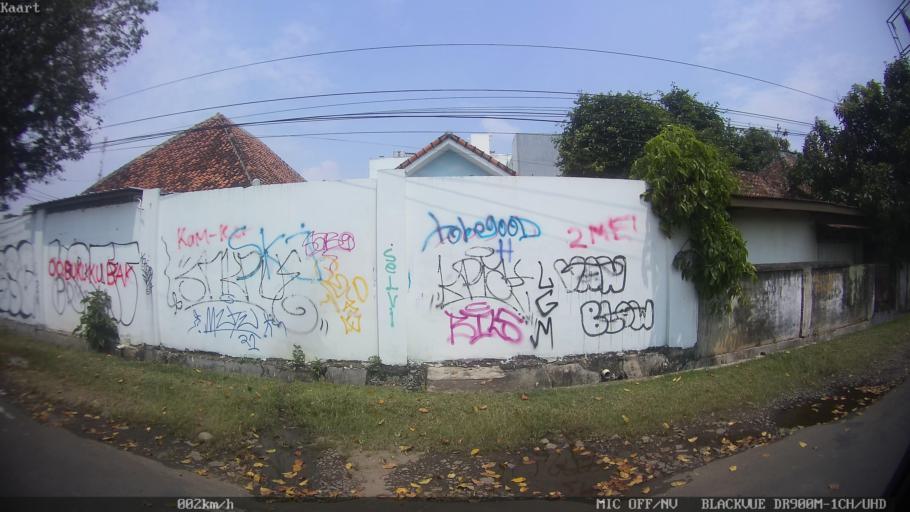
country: ID
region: Lampung
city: Bandarlampung
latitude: -5.4301
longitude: 105.2718
